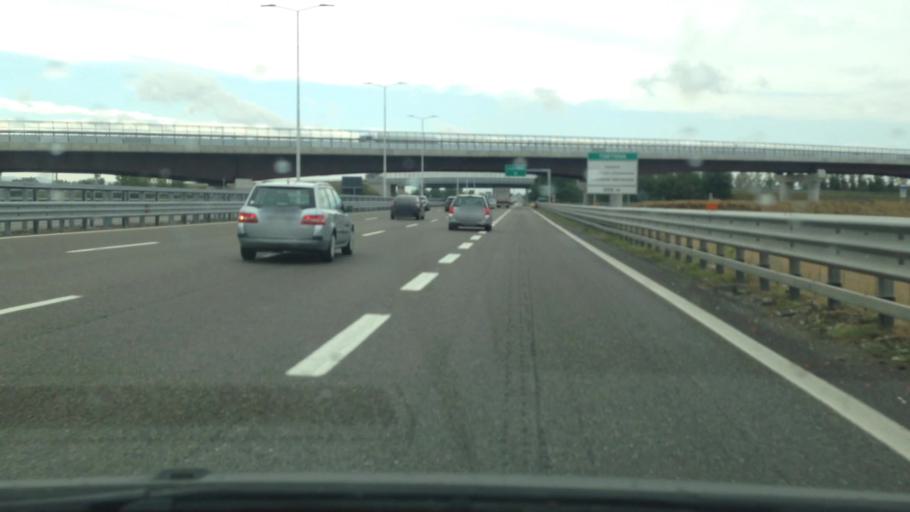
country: IT
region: Piedmont
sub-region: Provincia di Alessandria
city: Tortona
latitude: 44.9116
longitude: 8.8438
